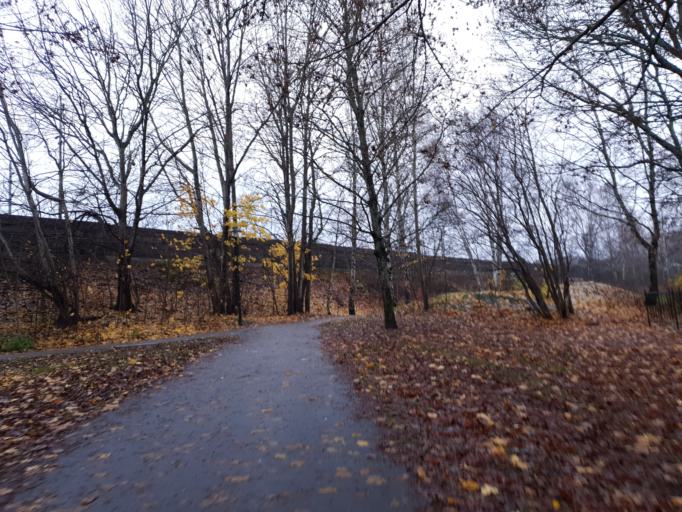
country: SE
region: Stockholm
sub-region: Stockholms Kommun
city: Arsta
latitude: 59.2410
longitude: 18.0867
